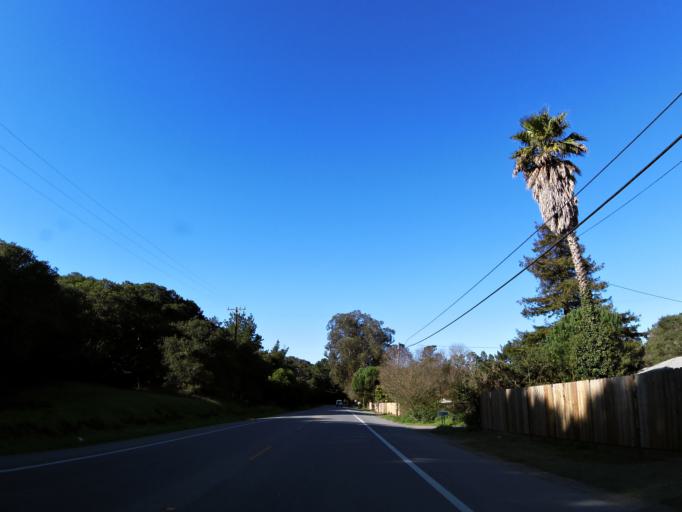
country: US
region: California
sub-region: Monterey County
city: Las Lomas
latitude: 36.8409
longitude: -121.6870
